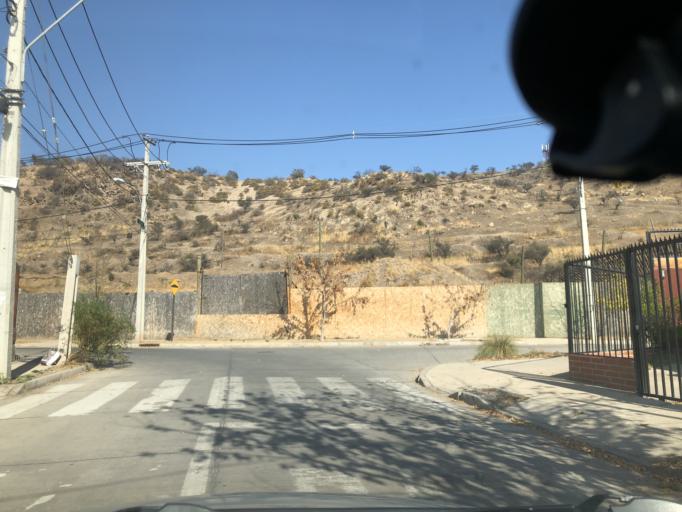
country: CL
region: Santiago Metropolitan
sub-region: Provincia de Cordillera
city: Puente Alto
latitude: -33.5995
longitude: -70.5520
